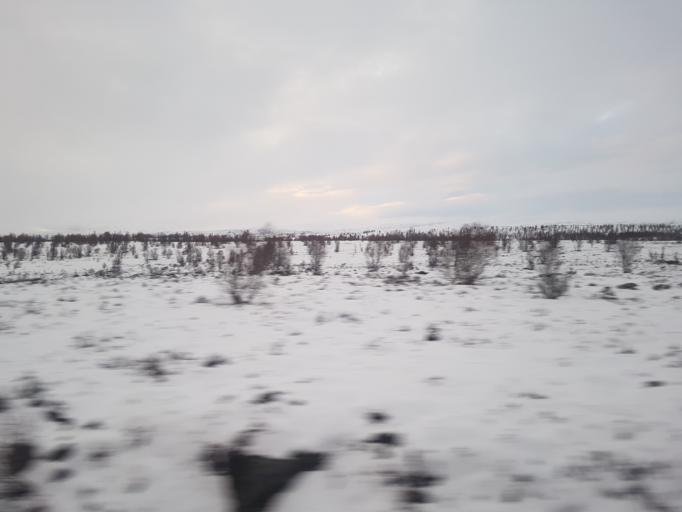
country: NO
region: Oppland
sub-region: Dovre
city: Dovre
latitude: 62.1454
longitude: 9.3370
